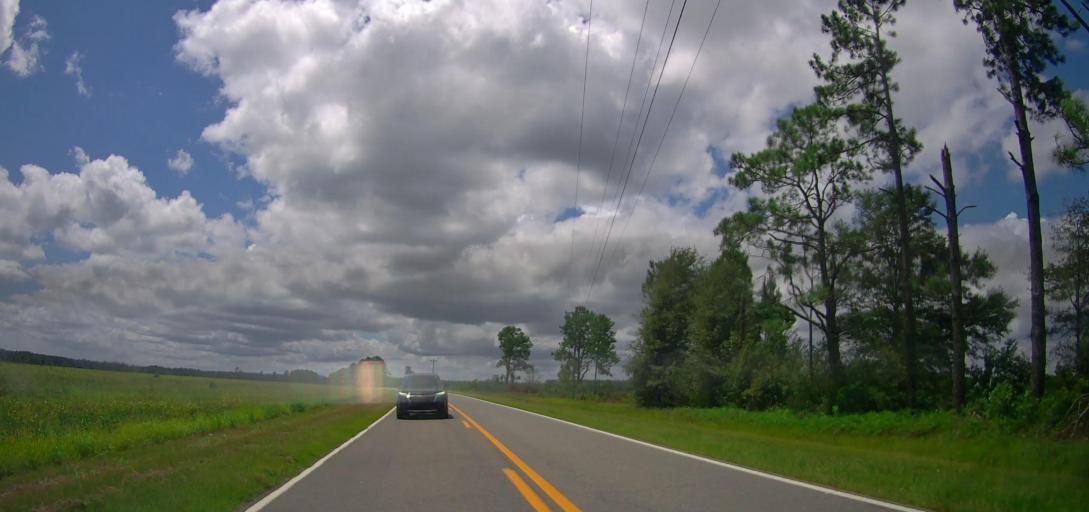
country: US
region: Georgia
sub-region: Irwin County
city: Ocilla
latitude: 31.6469
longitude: -83.2991
